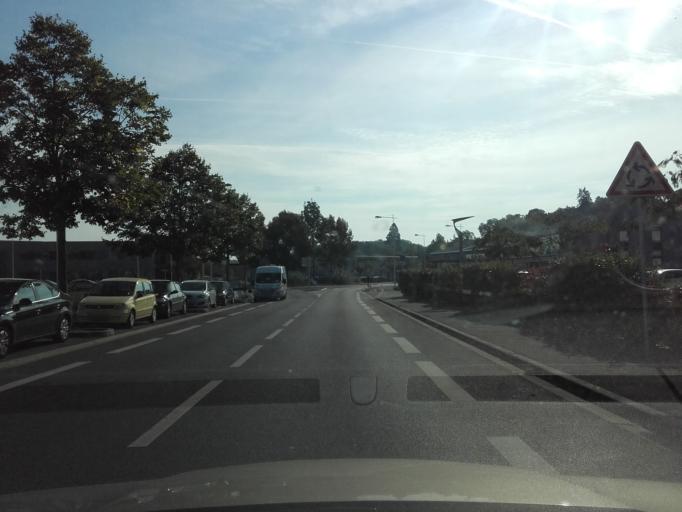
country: FR
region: Centre
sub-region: Departement d'Indre-et-Loire
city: Joue-les-Tours
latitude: 47.3637
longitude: 0.6785
